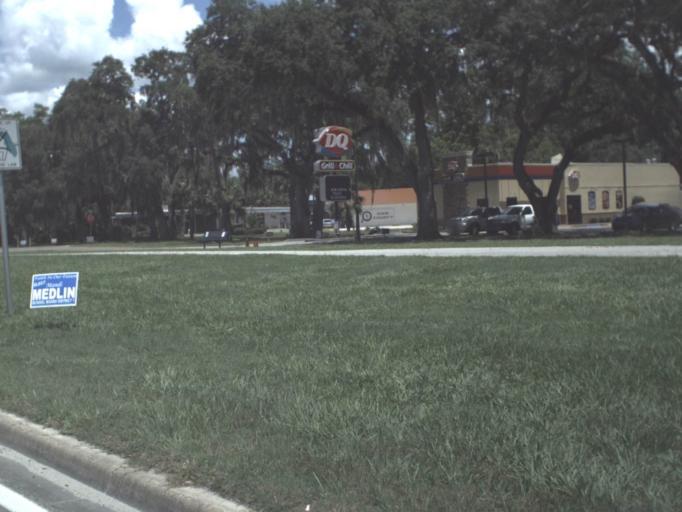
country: US
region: Florida
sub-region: Dixie County
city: Cross City
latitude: 29.6344
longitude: -83.1245
